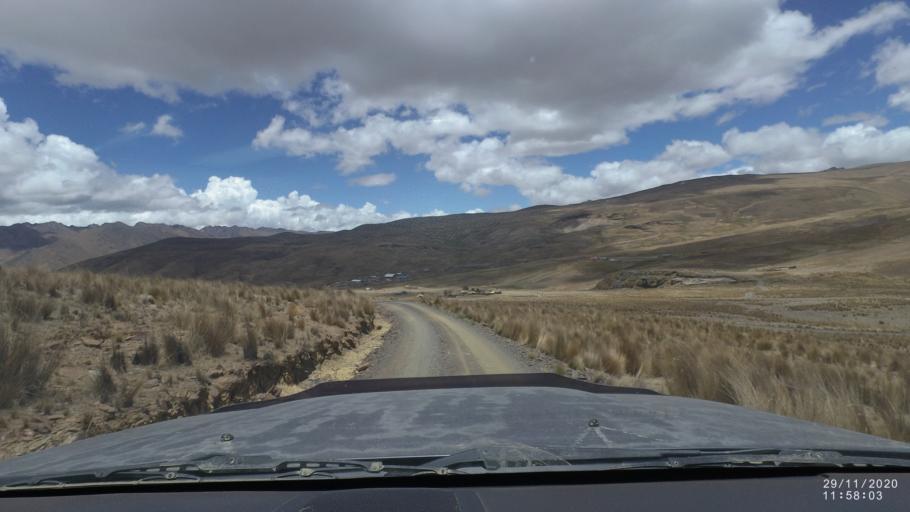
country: BO
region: Cochabamba
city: Cochabamba
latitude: -17.1568
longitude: -66.2752
